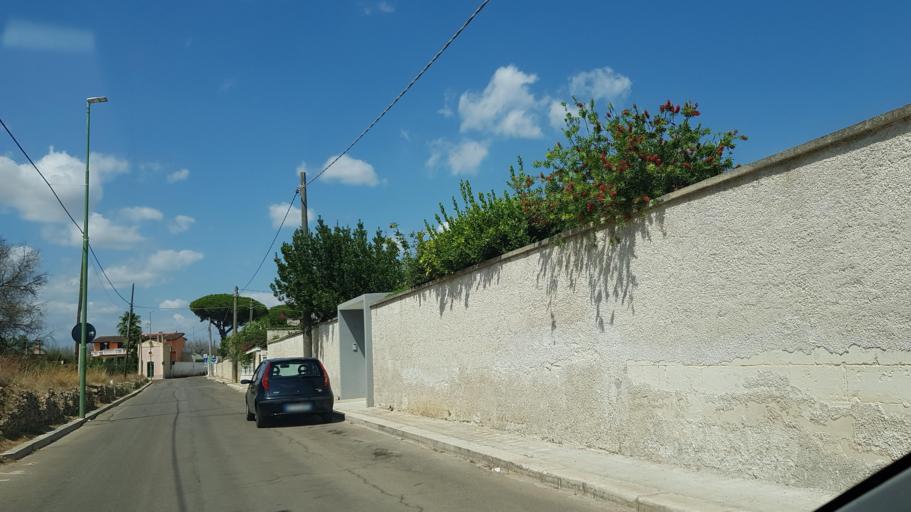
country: IT
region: Apulia
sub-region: Provincia di Lecce
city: Trepuzzi
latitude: 40.4080
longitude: 18.0603
